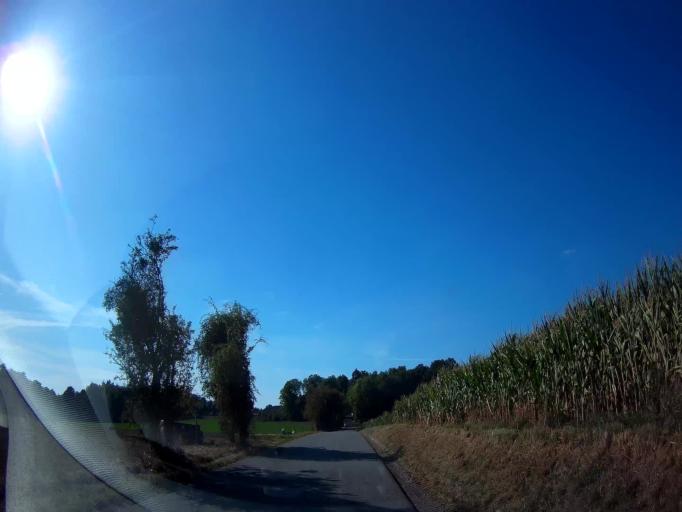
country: BE
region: Wallonia
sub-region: Province de Namur
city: Dinant
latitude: 50.2500
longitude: 4.9413
